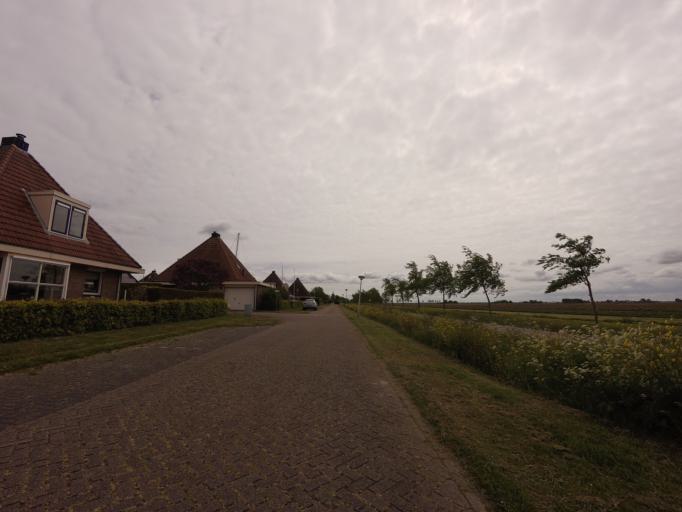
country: NL
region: Friesland
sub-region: Sudwest Fryslan
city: Woudsend
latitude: 52.9480
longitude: 5.6207
